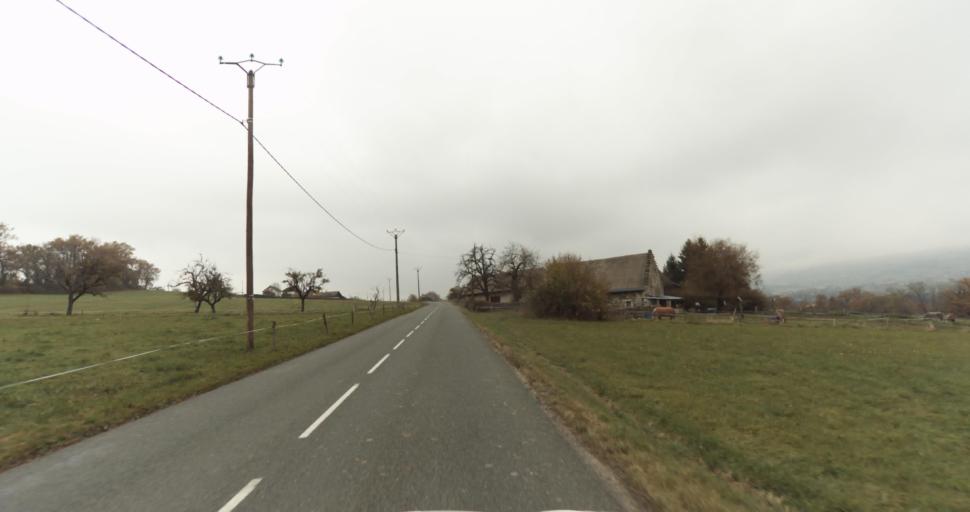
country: FR
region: Rhone-Alpes
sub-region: Departement de la Haute-Savoie
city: Cusy
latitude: 45.7808
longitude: 6.0155
